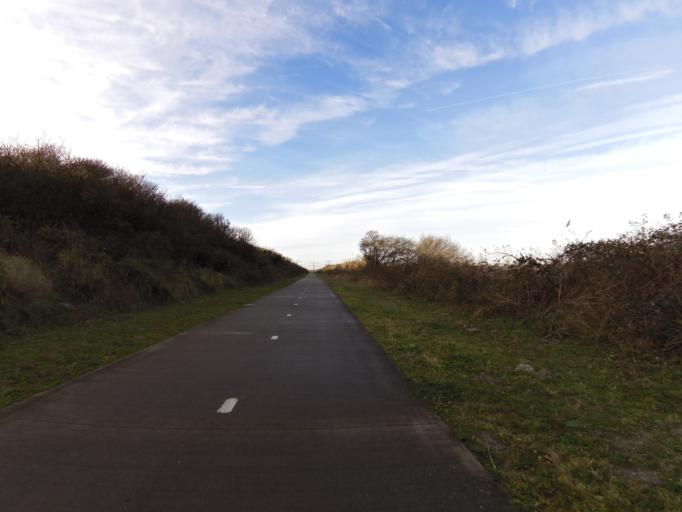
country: NL
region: South Holland
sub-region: Gemeente Rotterdam
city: Hoek van Holland
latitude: 51.9203
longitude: 4.0541
